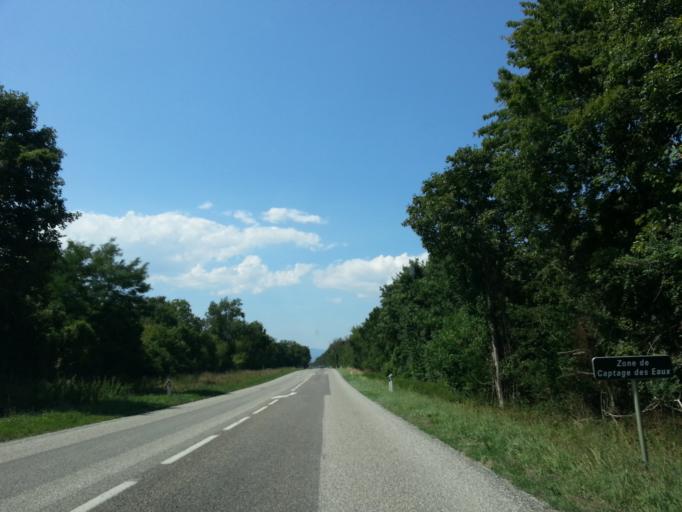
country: FR
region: Alsace
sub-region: Departement du Haut-Rhin
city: Widensolen
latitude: 48.0390
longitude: 7.4788
